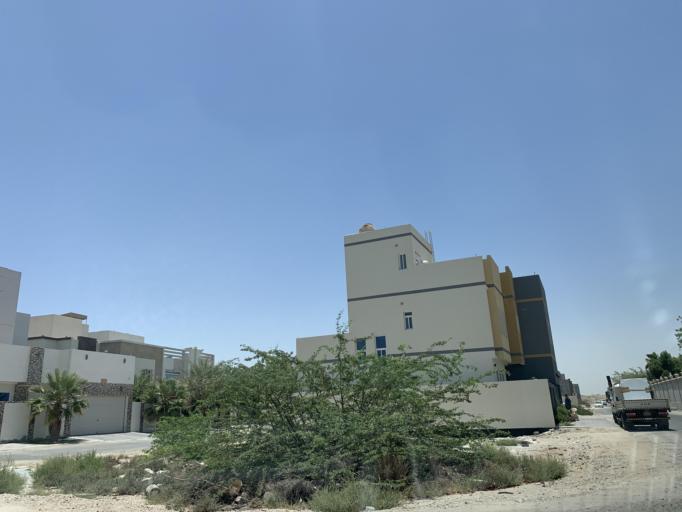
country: BH
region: Manama
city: Jidd Hafs
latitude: 26.2246
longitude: 50.4810
